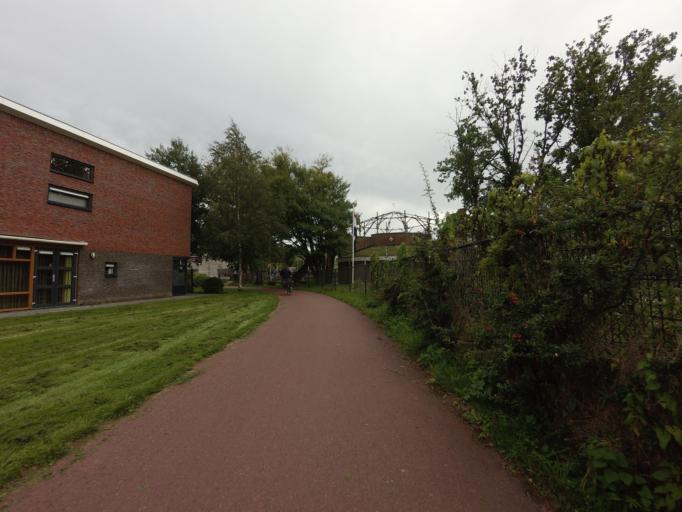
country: NL
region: Friesland
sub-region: Gemeente Leeuwarden
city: Bilgaard
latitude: 53.2165
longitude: 5.7917
